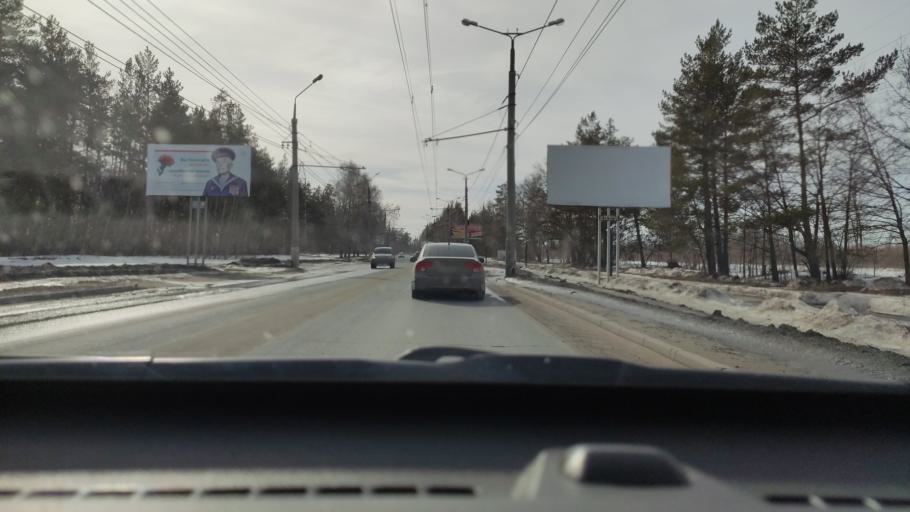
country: RU
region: Samara
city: Tol'yatti
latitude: 53.4959
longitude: 49.3856
